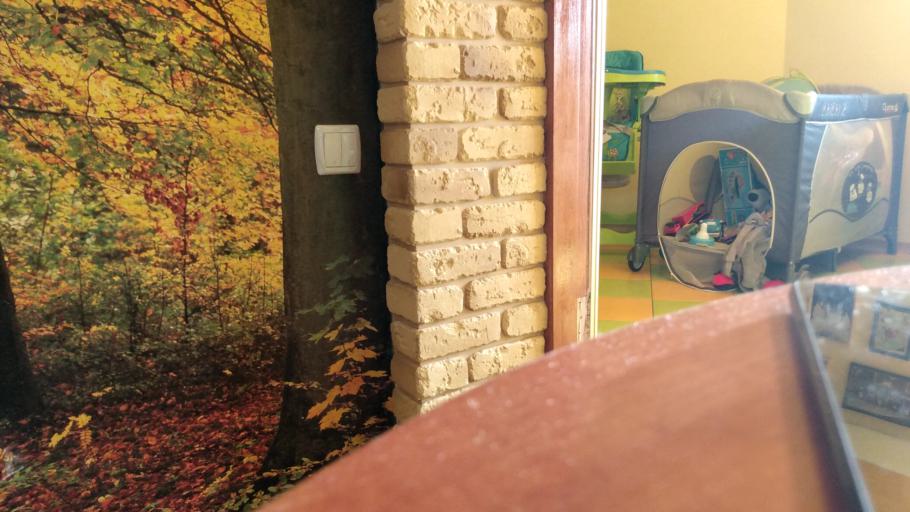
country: RU
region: Tverskaya
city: Vasil'yevskiy Mokh
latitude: 57.0250
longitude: 35.8342
